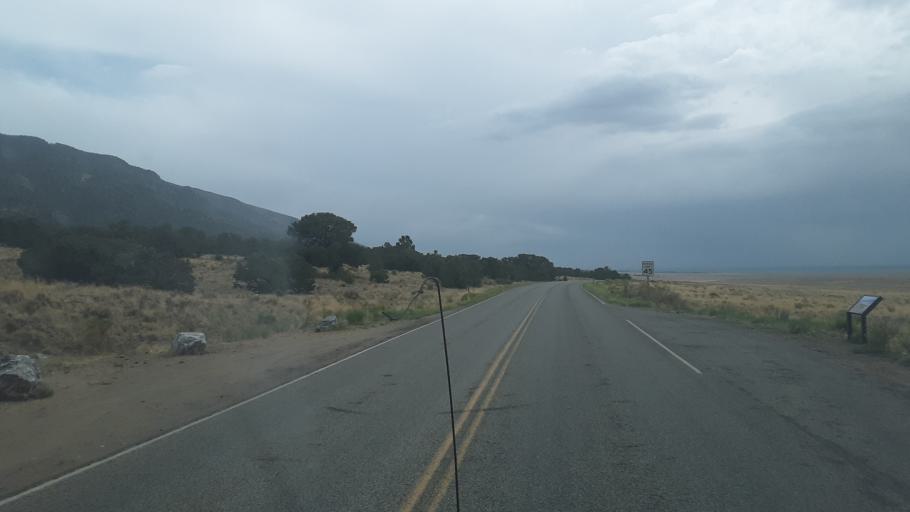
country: US
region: Colorado
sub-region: Alamosa County
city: Alamosa East
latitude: 37.7223
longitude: -105.5214
